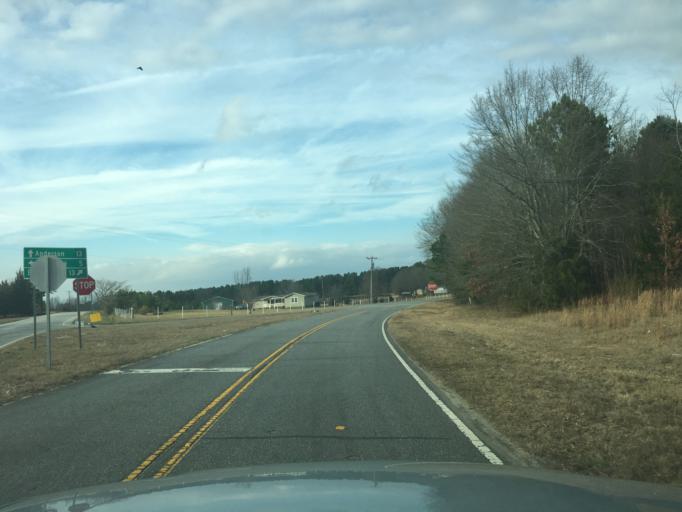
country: US
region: South Carolina
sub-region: Abbeville County
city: Lake Secession
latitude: 34.3624
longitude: -82.5200
